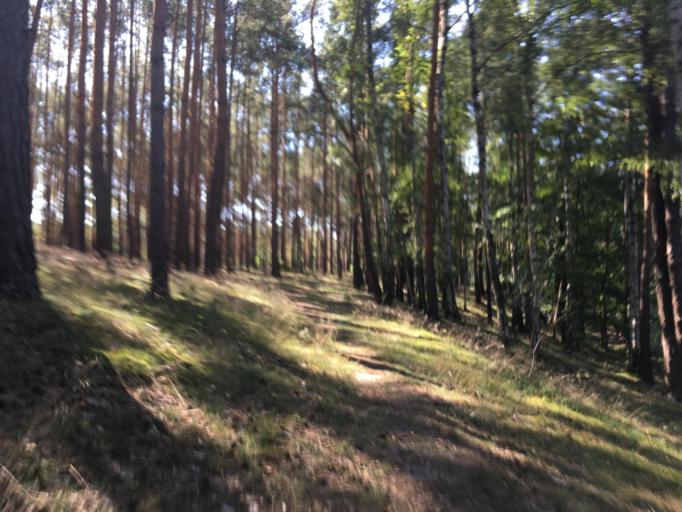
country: DE
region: Brandenburg
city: Gross Koris
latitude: 52.2049
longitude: 13.7457
